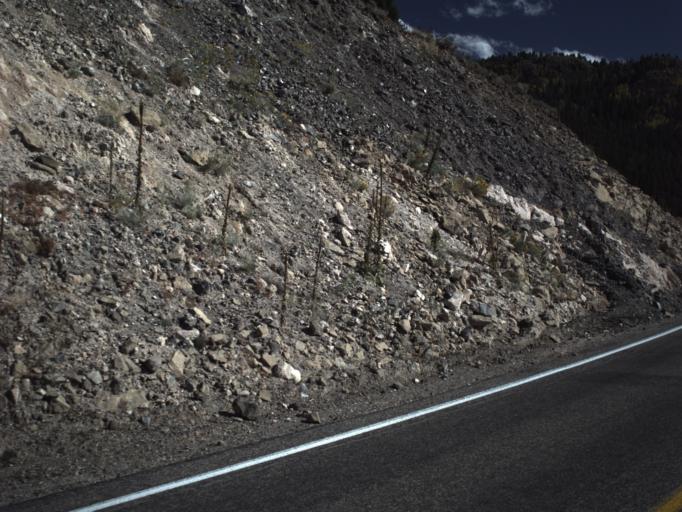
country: US
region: Utah
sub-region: Garfield County
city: Panguitch
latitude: 37.7202
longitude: -112.6262
